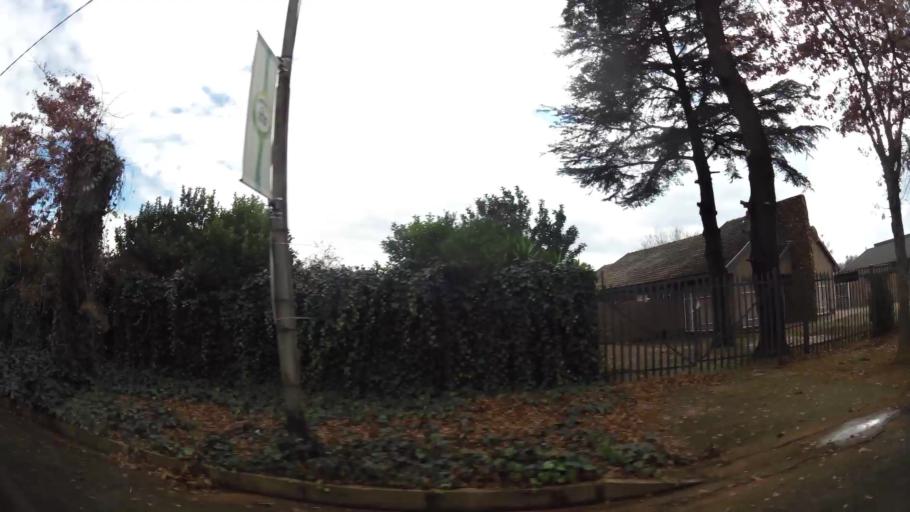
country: ZA
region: Gauteng
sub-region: Sedibeng District Municipality
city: Vereeniging
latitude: -26.6408
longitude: 27.9764
